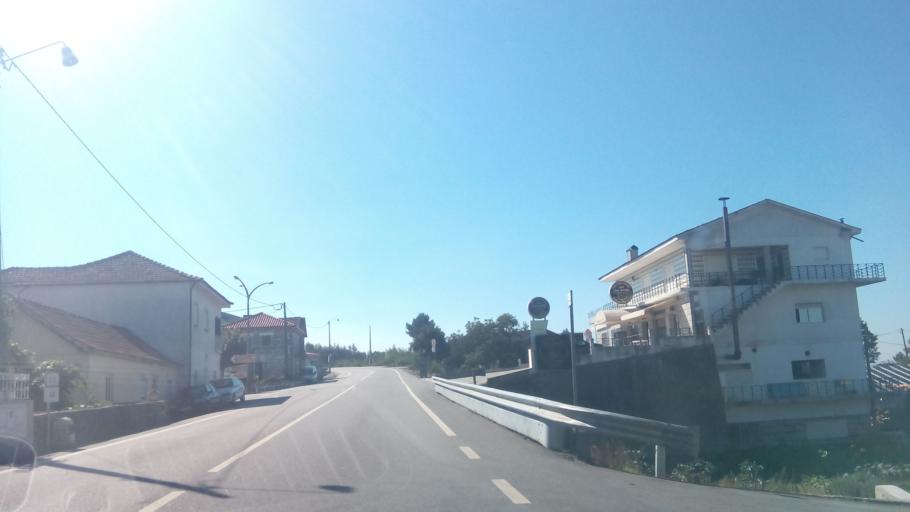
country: PT
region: Porto
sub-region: Amarante
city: Figueiro
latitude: 41.2834
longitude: -8.2035
